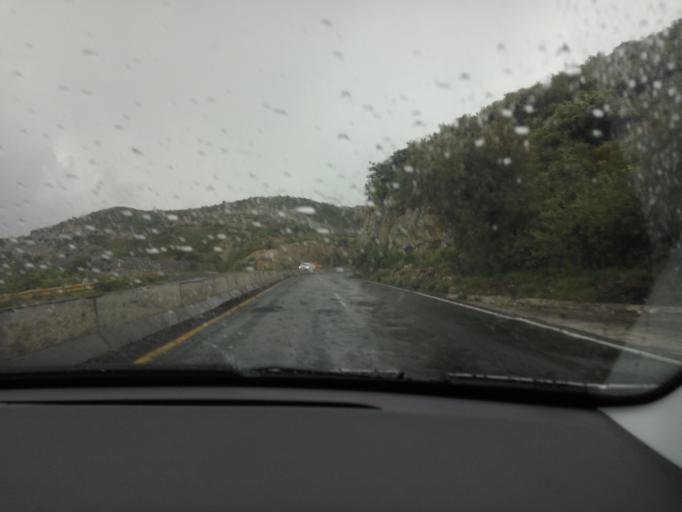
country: MX
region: Hidalgo
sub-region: Mineral de la Reforma
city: Colonia Militar
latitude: 20.1224
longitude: -98.6945
